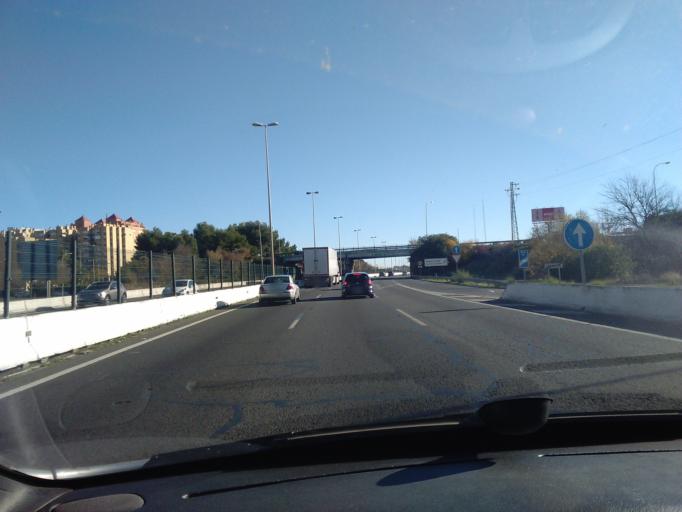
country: ES
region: Andalusia
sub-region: Provincia de Sevilla
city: Sevilla
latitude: 37.3860
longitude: -5.9250
